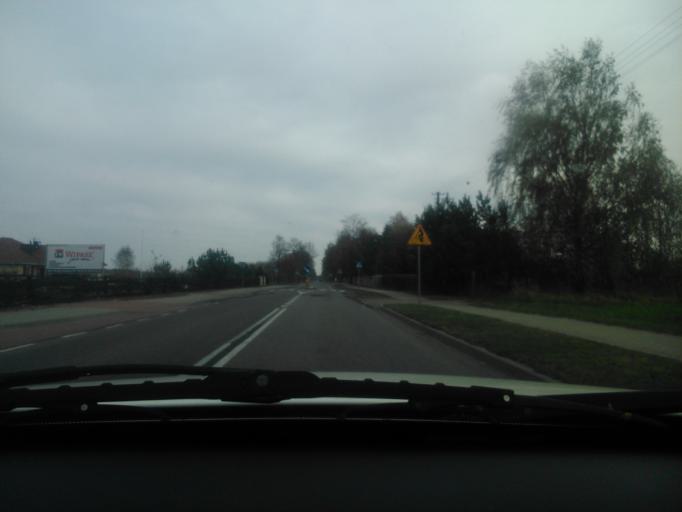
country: PL
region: Masovian Voivodeship
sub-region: Powiat mlawski
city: Szydlowo
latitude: 53.0768
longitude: 20.5244
